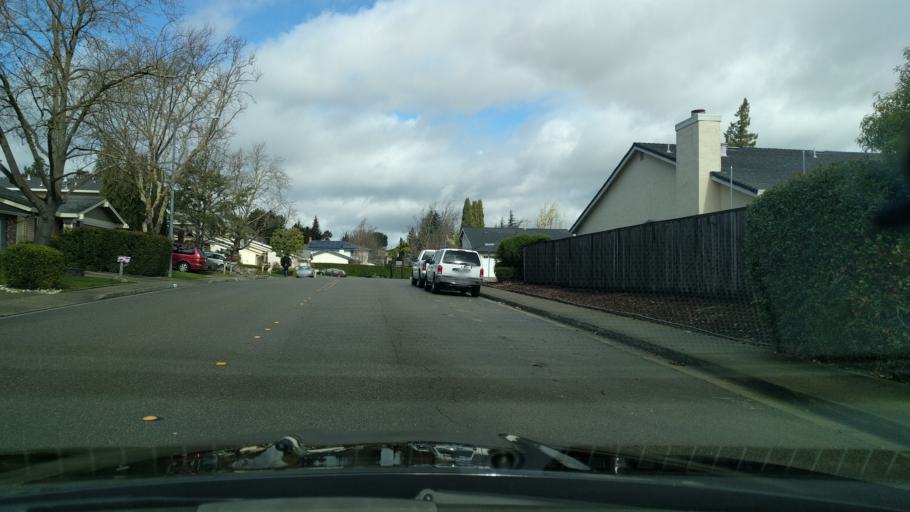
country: US
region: California
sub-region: Contra Costa County
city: San Ramon
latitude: 37.7633
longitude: -121.9717
